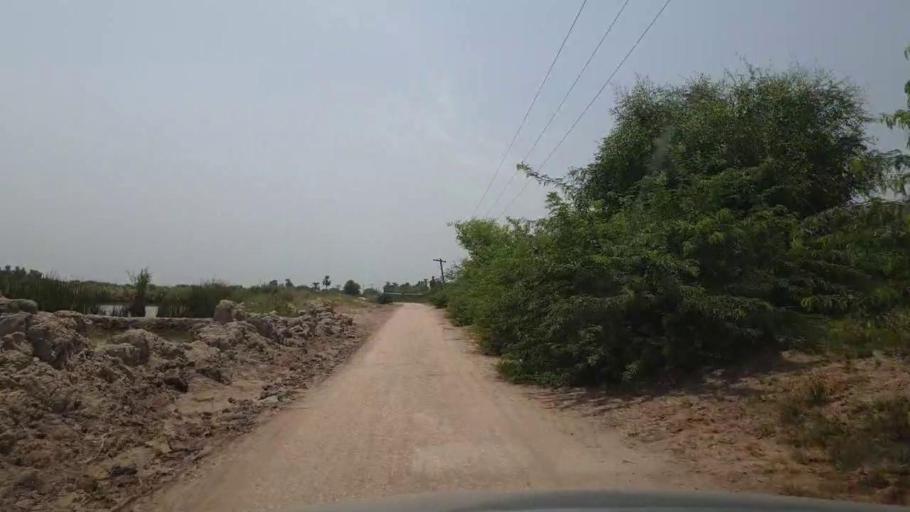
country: PK
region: Sindh
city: Garhi Yasin
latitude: 27.8817
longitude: 68.4953
